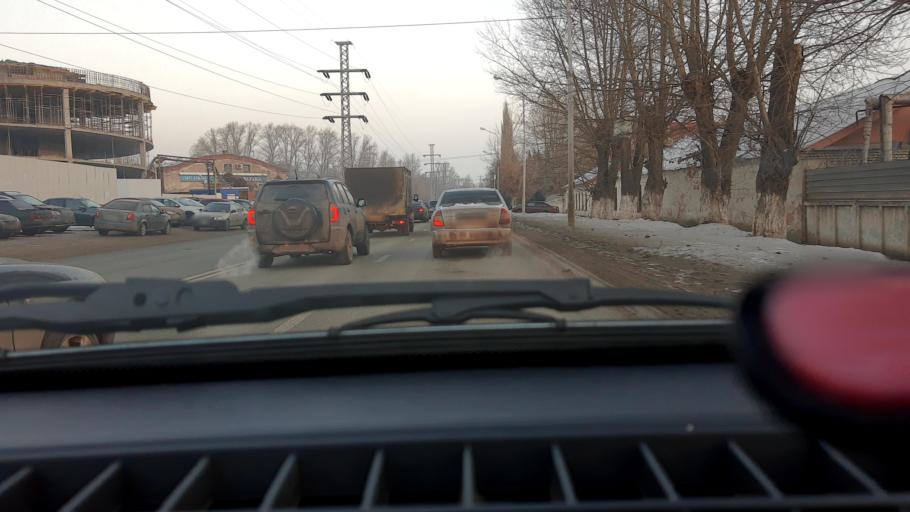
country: RU
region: Bashkortostan
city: Ufa
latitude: 54.7832
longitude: 56.0547
